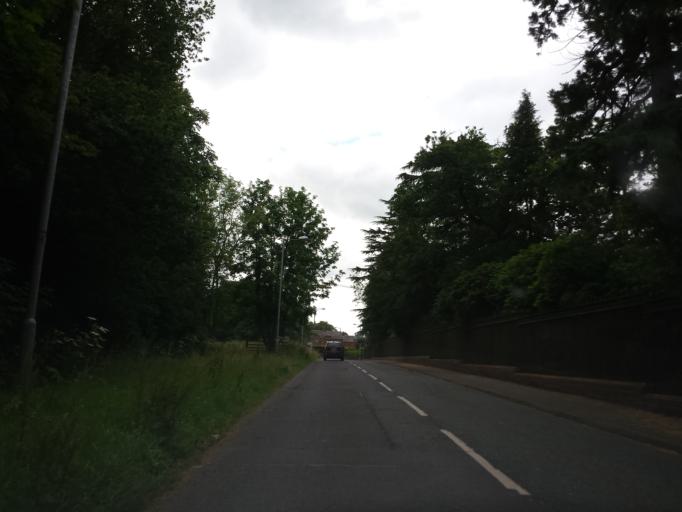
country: GB
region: Scotland
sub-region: Dumfries and Galloway
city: Dumfries
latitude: 55.0540
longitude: -3.5944
